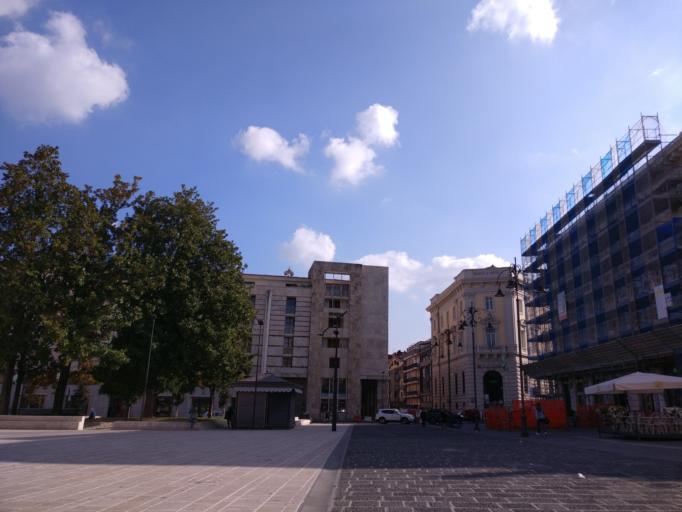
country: IT
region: Campania
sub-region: Provincia di Avellino
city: Avellino
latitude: 40.9146
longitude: 14.7919
